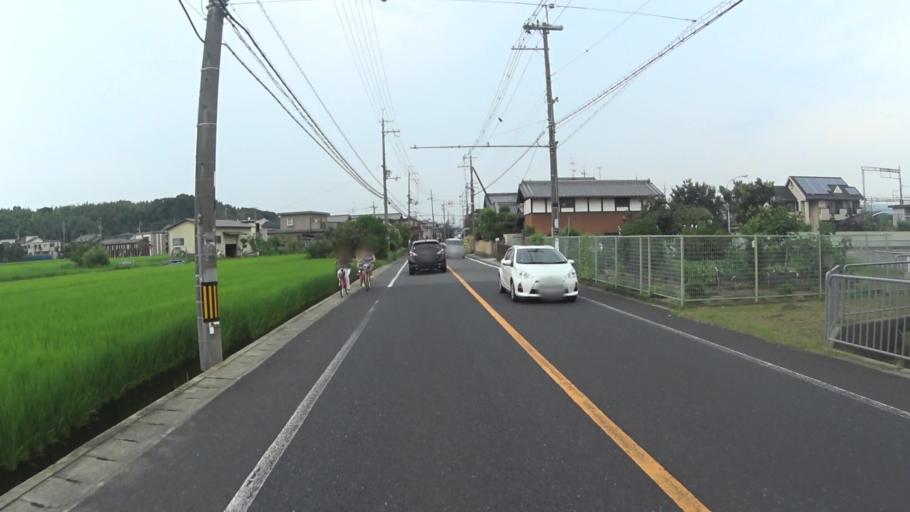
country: JP
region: Kyoto
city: Tanabe
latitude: 34.7884
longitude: 135.7865
